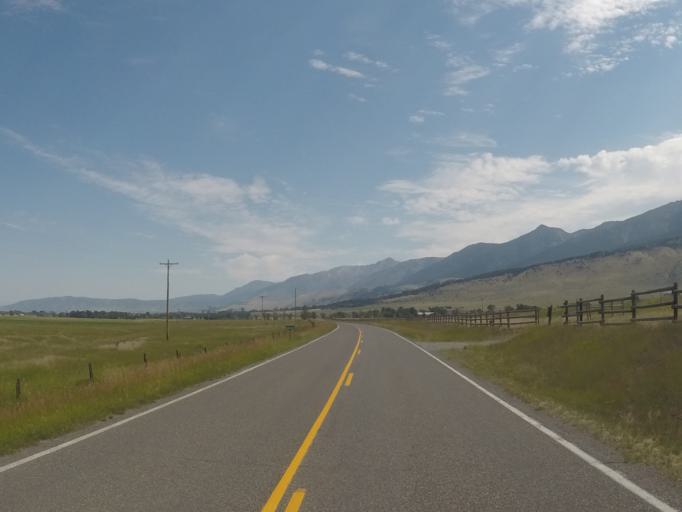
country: US
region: Montana
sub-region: Park County
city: Livingston
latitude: 45.4257
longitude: -110.6219
